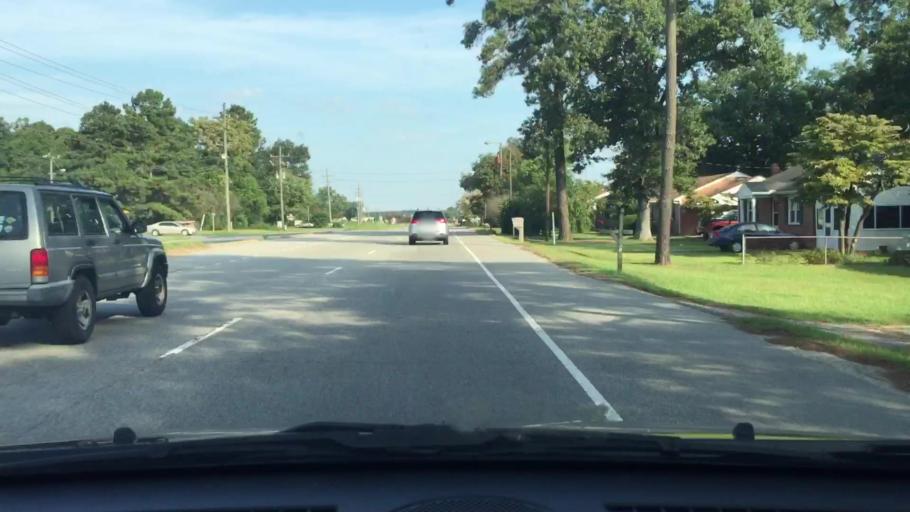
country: US
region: Virginia
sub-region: Isle of Wight County
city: Carrollton
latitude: 36.9438
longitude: -76.5910
